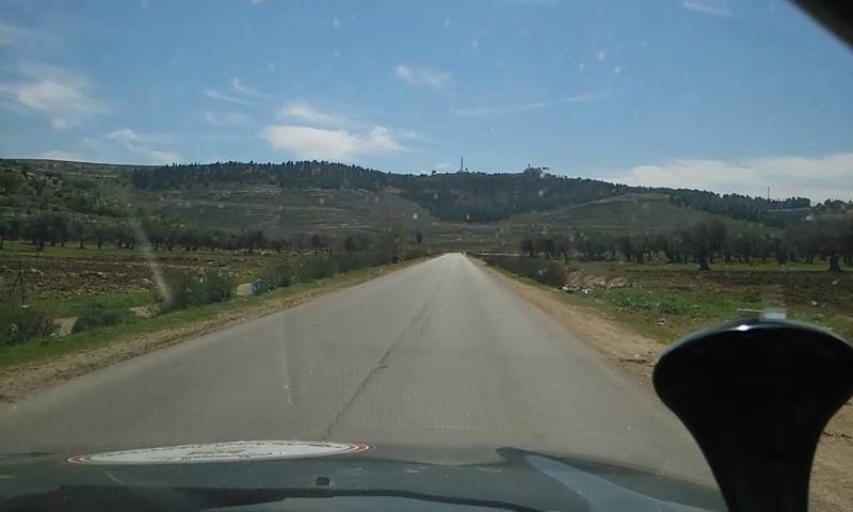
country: PS
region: West Bank
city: Al Jib
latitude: 31.8460
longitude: 35.1805
